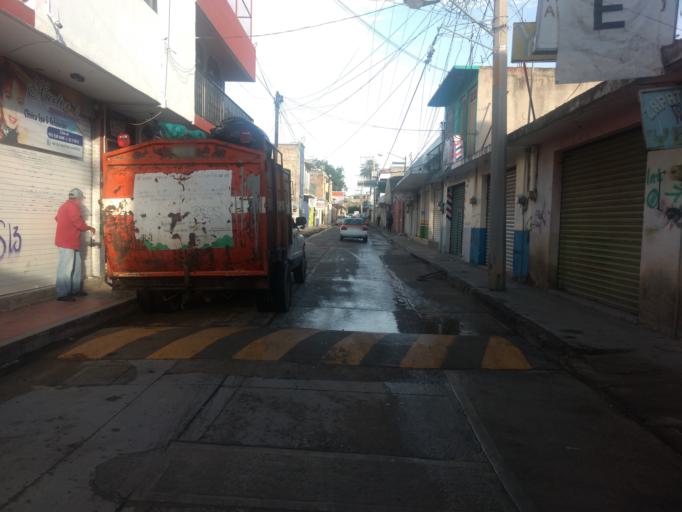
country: MX
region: Oaxaca
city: Ciudad de Huajuapam de Leon
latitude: 17.8081
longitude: -97.7773
